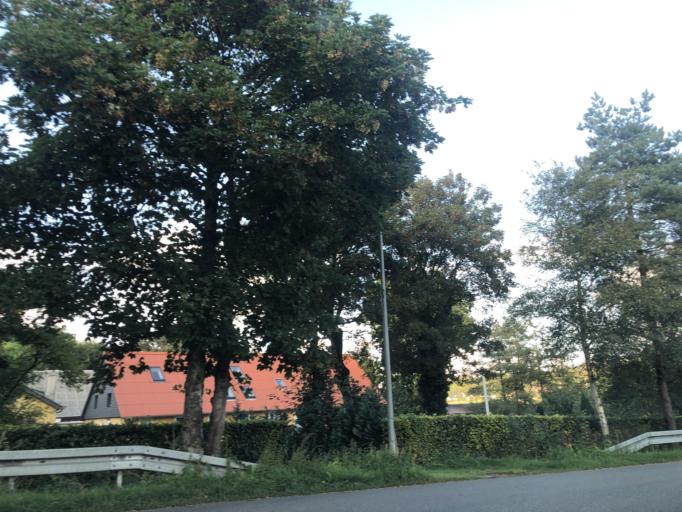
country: DK
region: North Denmark
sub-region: Alborg Kommune
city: Svenstrup
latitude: 56.9419
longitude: 9.8057
